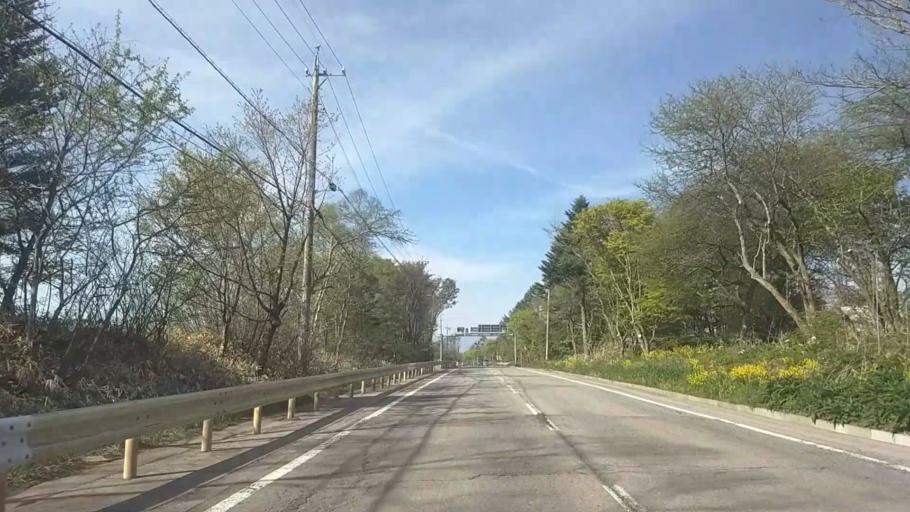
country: JP
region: Yamanashi
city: Nirasaki
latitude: 35.9516
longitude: 138.4593
